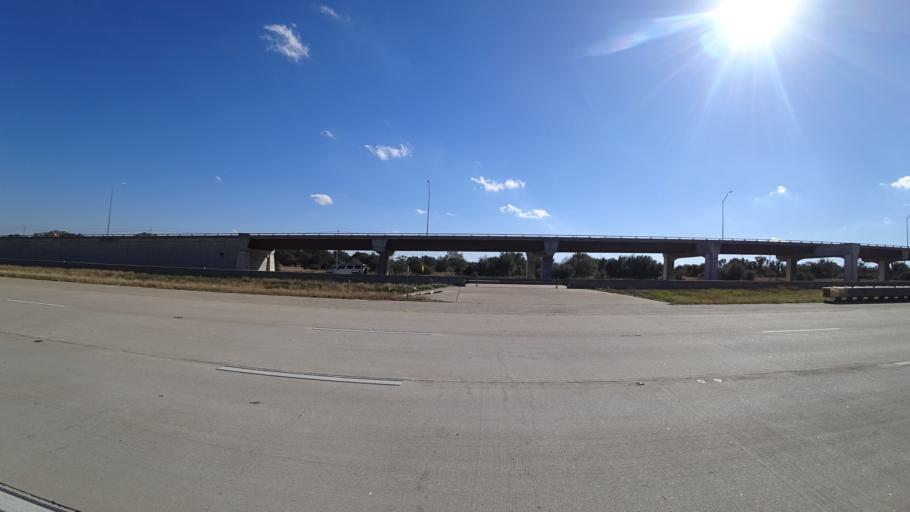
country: US
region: Texas
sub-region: Williamson County
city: Brushy Creek
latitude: 30.4798
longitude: -97.7551
